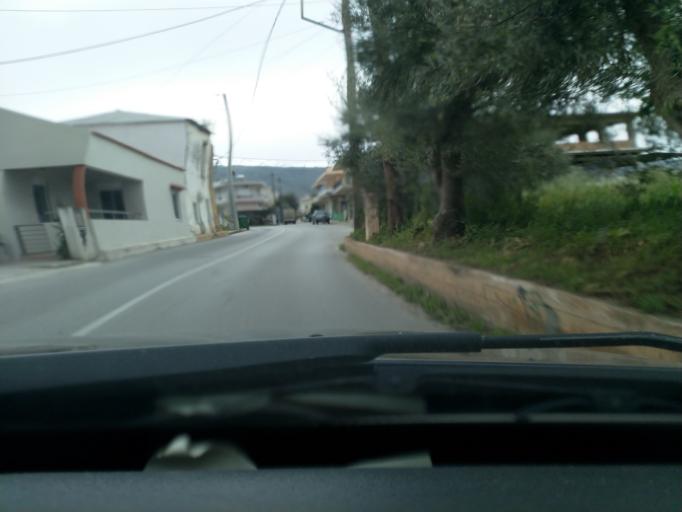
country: GR
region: Crete
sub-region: Nomos Chanias
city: Chania
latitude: 35.4981
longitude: 24.0217
